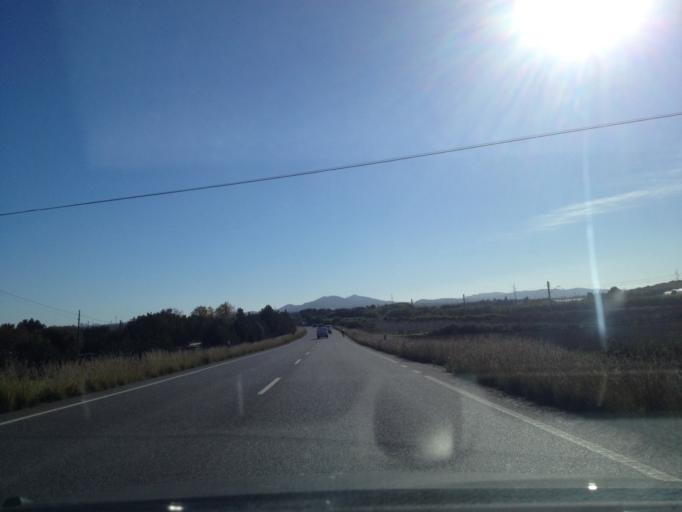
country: ES
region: Balearic Islands
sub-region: Illes Balears
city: Petra
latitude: 39.5917
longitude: 3.1381
